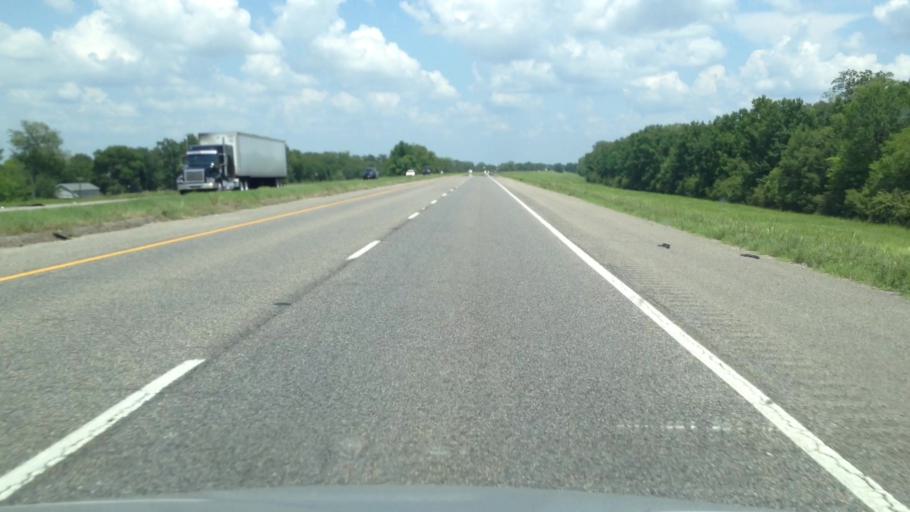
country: US
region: Louisiana
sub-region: Saint Landry Parish
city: Port Barre
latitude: 30.5483
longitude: -91.8543
